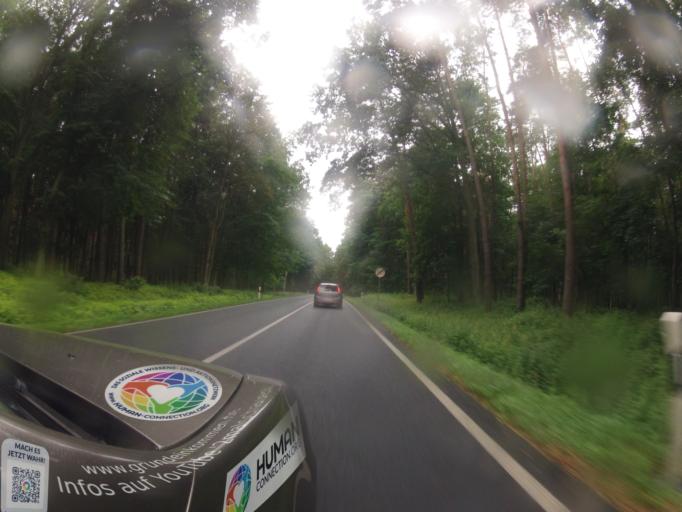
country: DE
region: Mecklenburg-Vorpommern
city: Usedom
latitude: 53.9081
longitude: 14.0123
